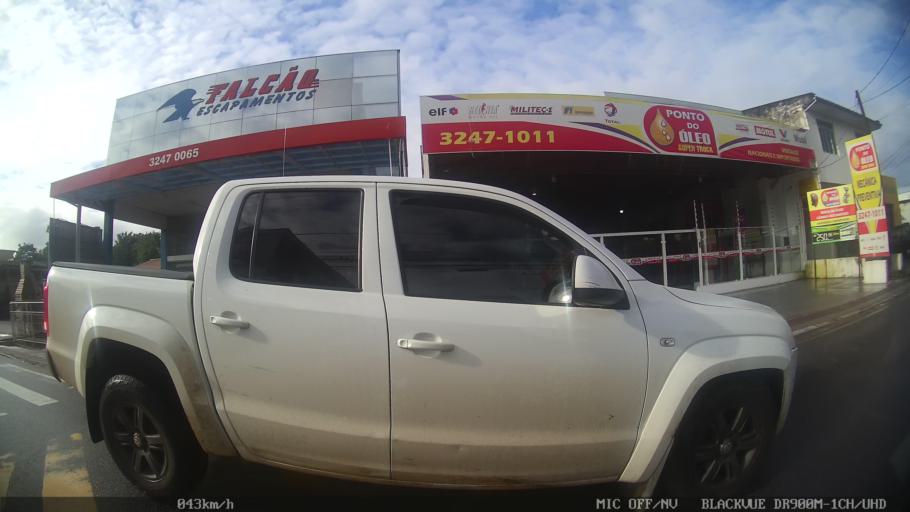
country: BR
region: Santa Catarina
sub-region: Sao Jose
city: Campinas
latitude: -27.6039
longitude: -48.6217
